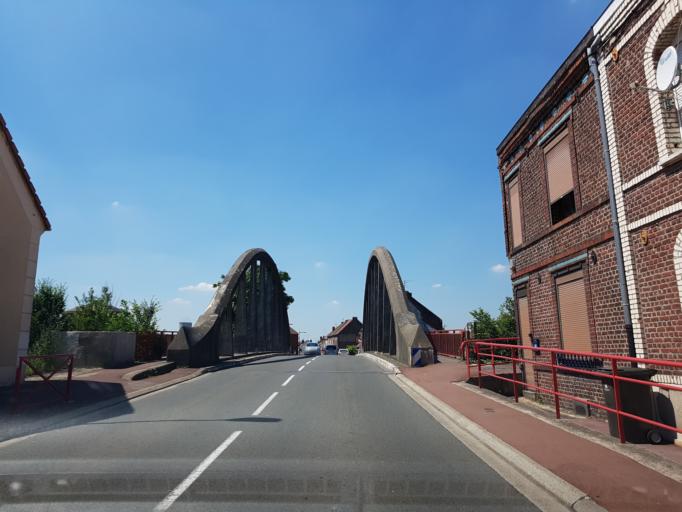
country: FR
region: Nord-Pas-de-Calais
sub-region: Departement du Nord
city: Lourches
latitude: 50.3124
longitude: 3.3435
